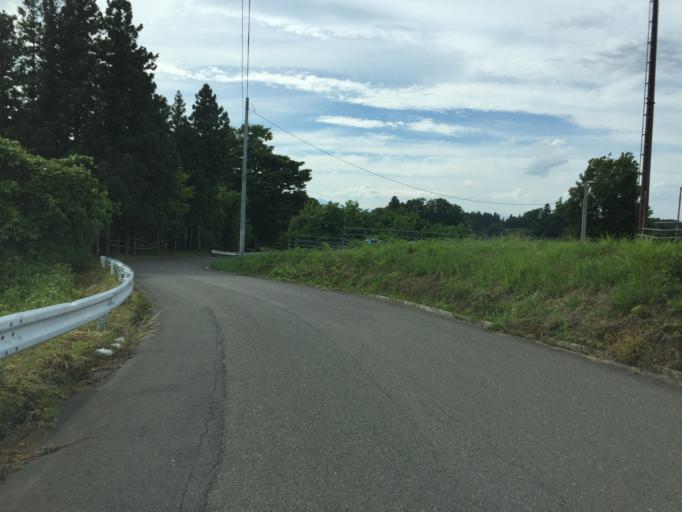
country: JP
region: Fukushima
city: Funehikimachi-funehiki
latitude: 37.5167
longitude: 140.5653
